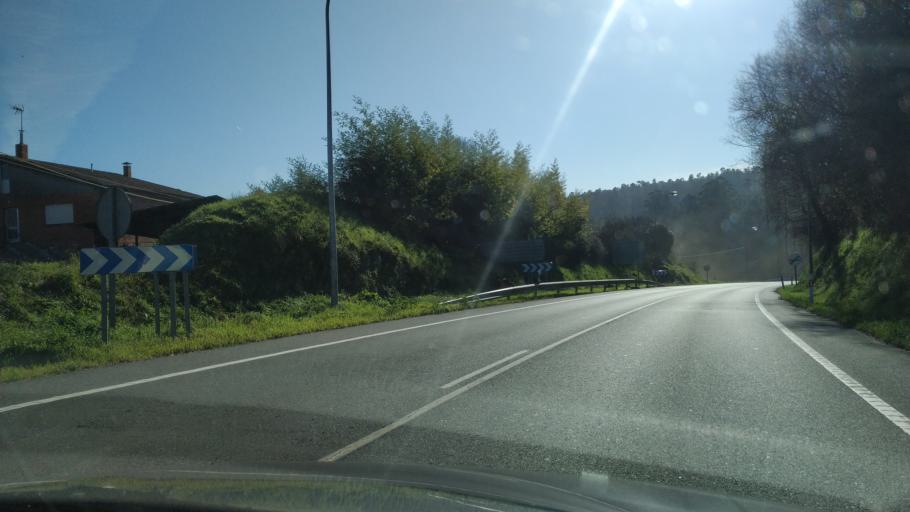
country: ES
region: Galicia
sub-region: Provincia de Pontevedra
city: Silleda
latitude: 42.7344
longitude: -8.3209
